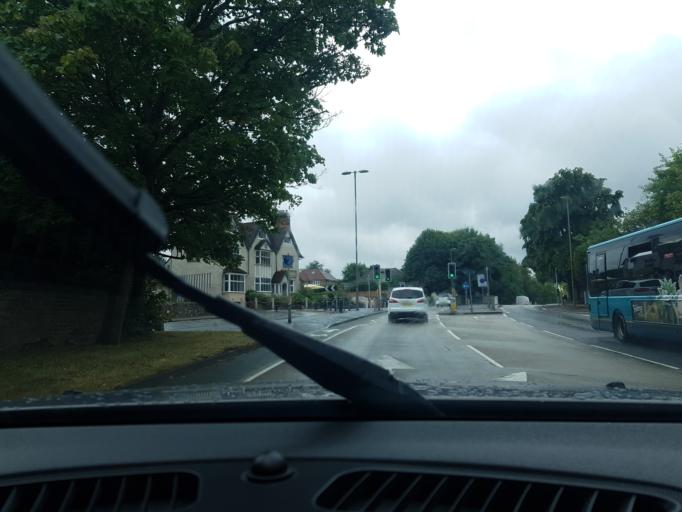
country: GB
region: England
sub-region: Surrey
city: Chilworth
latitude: 51.2467
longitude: -0.5272
